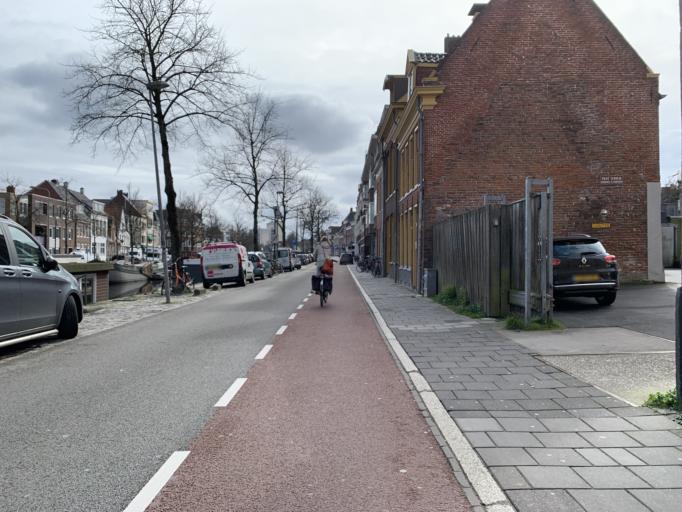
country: NL
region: Groningen
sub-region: Gemeente Groningen
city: Groningen
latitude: 53.2196
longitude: 6.5718
